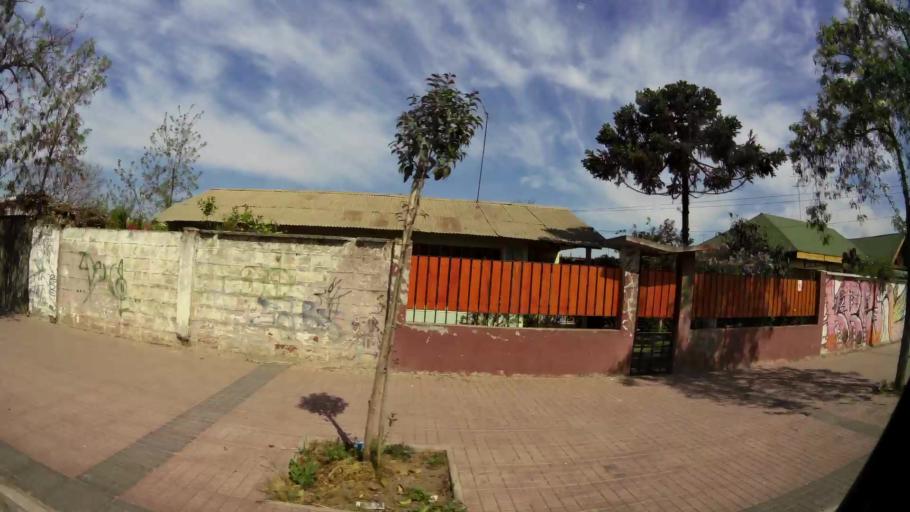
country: CL
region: Santiago Metropolitan
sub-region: Provincia de Talagante
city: Talagante
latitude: -33.6670
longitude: -70.9252
